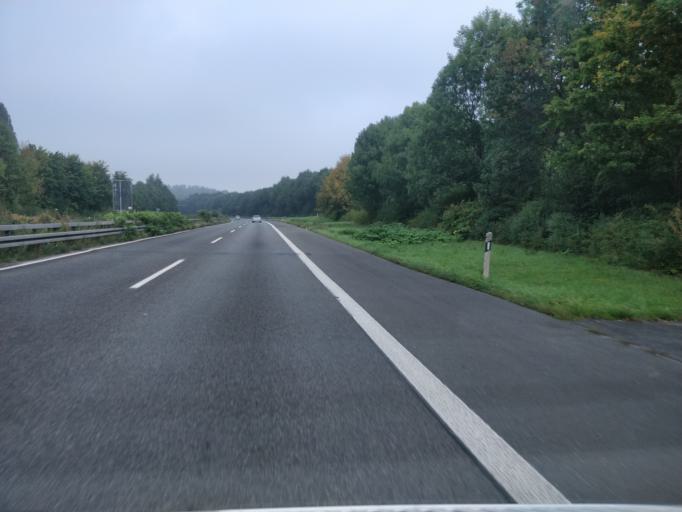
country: DE
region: North Rhine-Westphalia
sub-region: Regierungsbezirk Dusseldorf
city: Dinslaken
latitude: 51.5278
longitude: 6.7585
